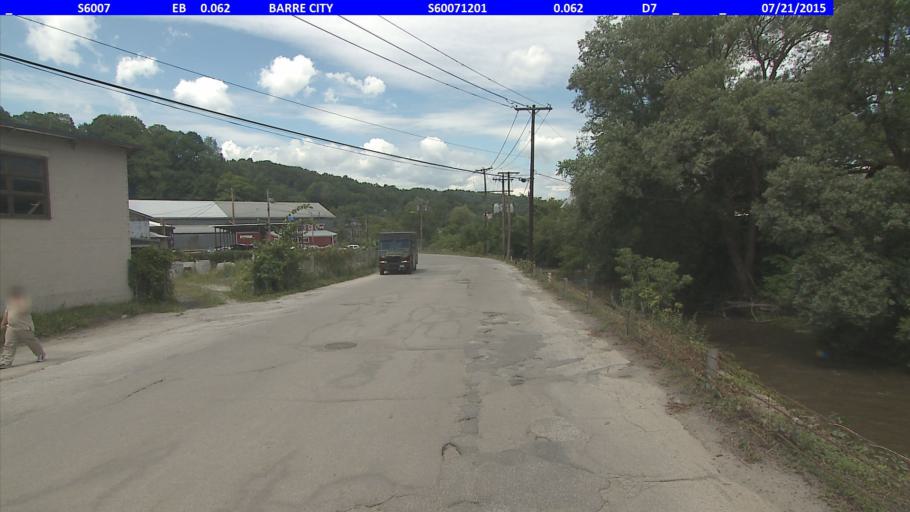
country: US
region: Vermont
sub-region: Washington County
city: Barre
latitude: 44.1972
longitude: -72.5043
